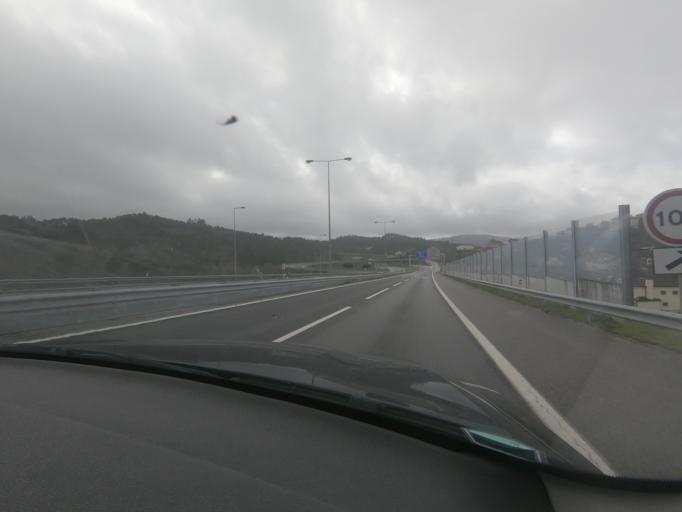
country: PT
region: Viseu
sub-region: Castro Daire
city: Castro Daire
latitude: 40.9050
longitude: -7.9086
